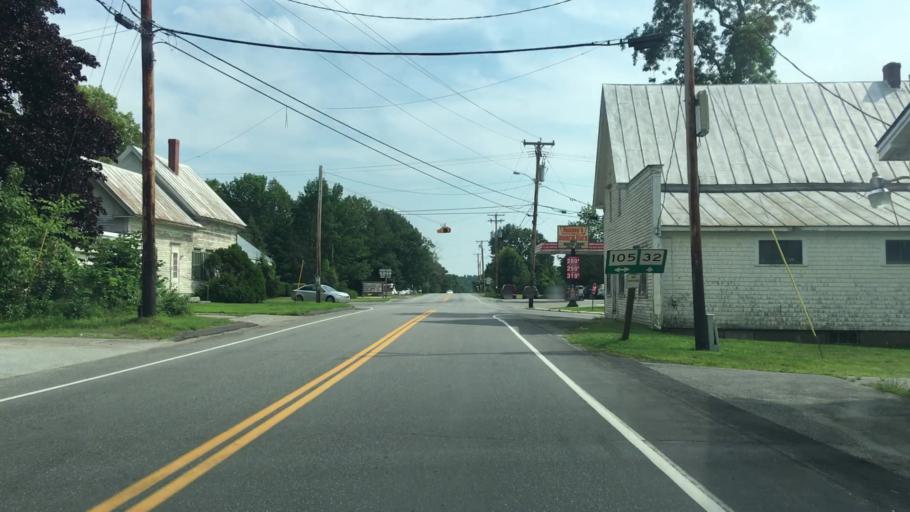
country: US
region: Maine
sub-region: Kennebec County
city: Windsor
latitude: 44.3112
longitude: -69.5812
